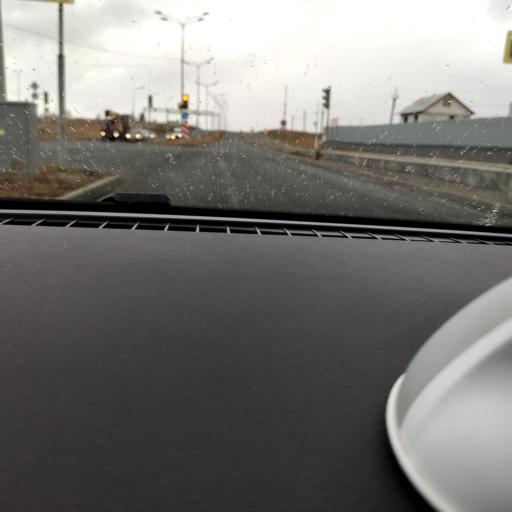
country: RU
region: Samara
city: Samara
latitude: 53.2818
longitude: 50.2422
